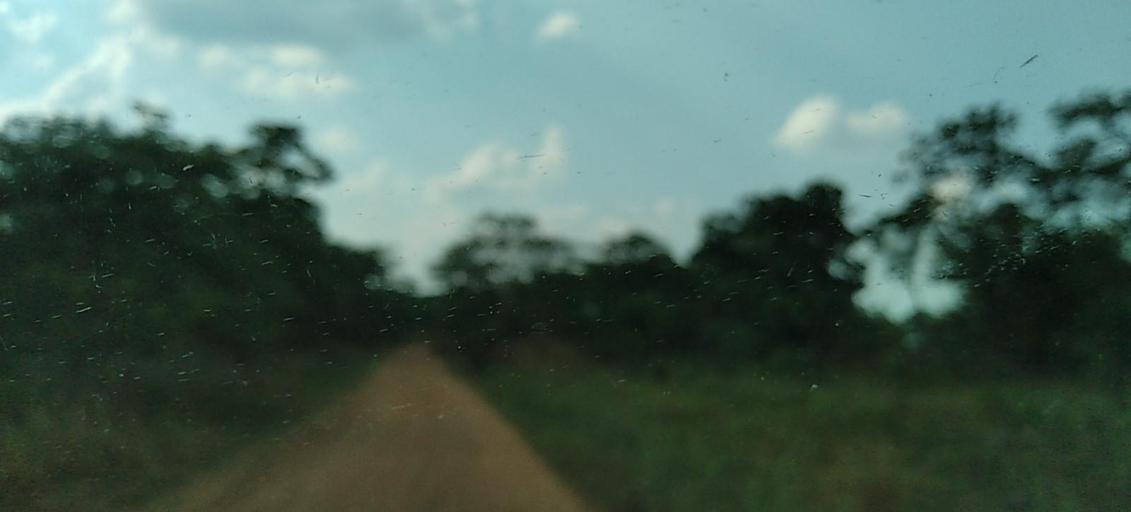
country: ZM
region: Copperbelt
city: Mpongwe
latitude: -13.5096
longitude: 28.0933
